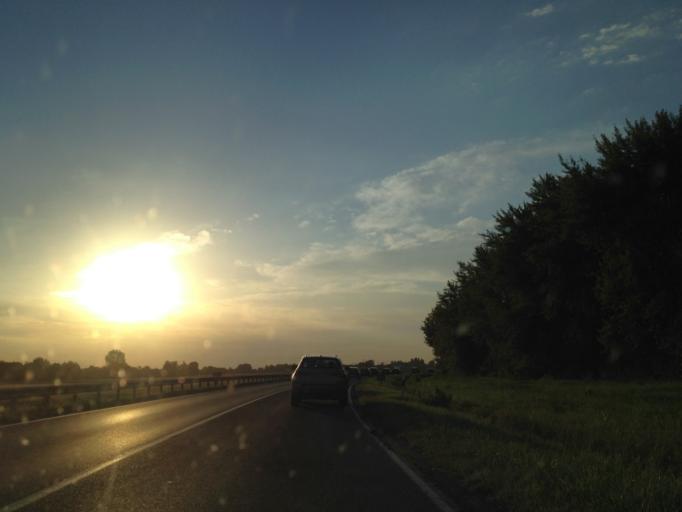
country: HU
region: Gyor-Moson-Sopron
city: Mosonmagyarovar
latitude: 47.8306
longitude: 17.3000
